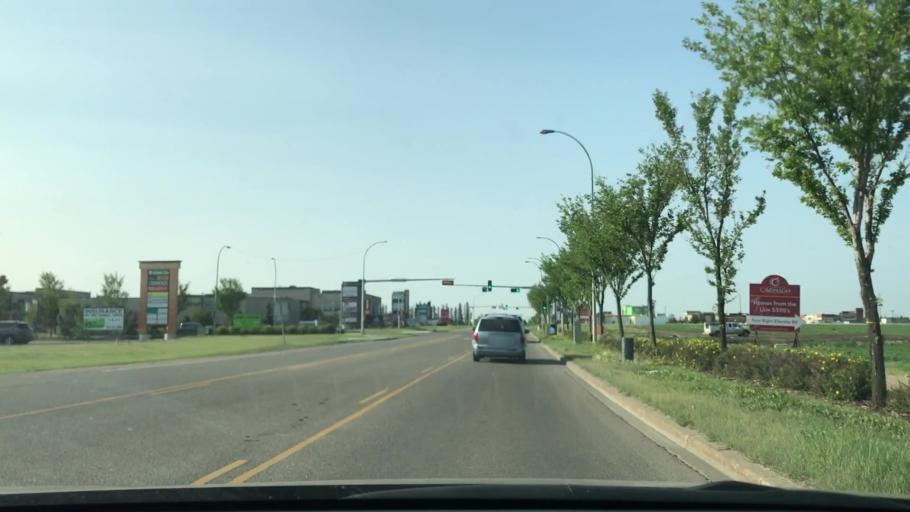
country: CA
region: Alberta
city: Beaumont
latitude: 53.4304
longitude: -113.4800
